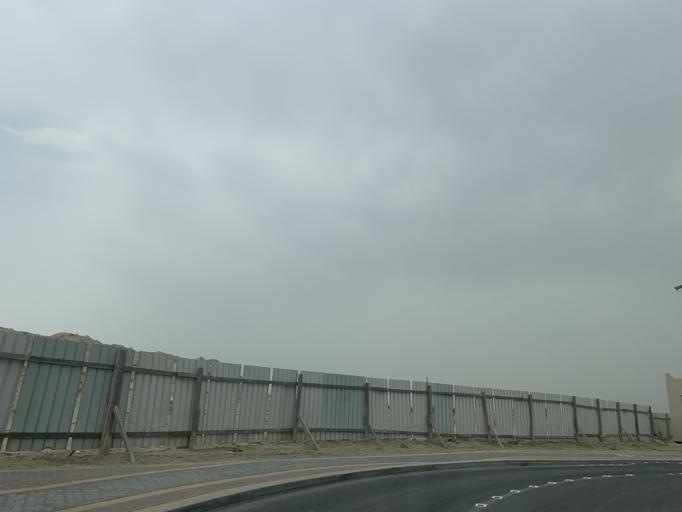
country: BH
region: Northern
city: Madinat `Isa
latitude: 26.1683
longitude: 50.5095
